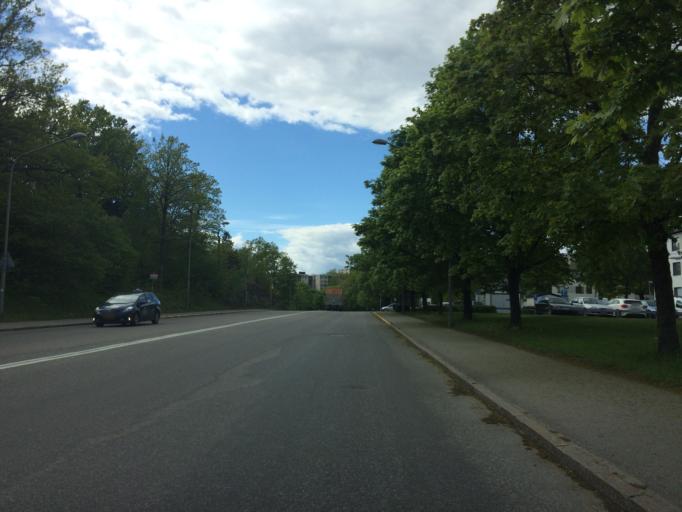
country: SE
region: Stockholm
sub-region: Huddinge Kommun
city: Segeltorp
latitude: 59.2737
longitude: 17.8994
